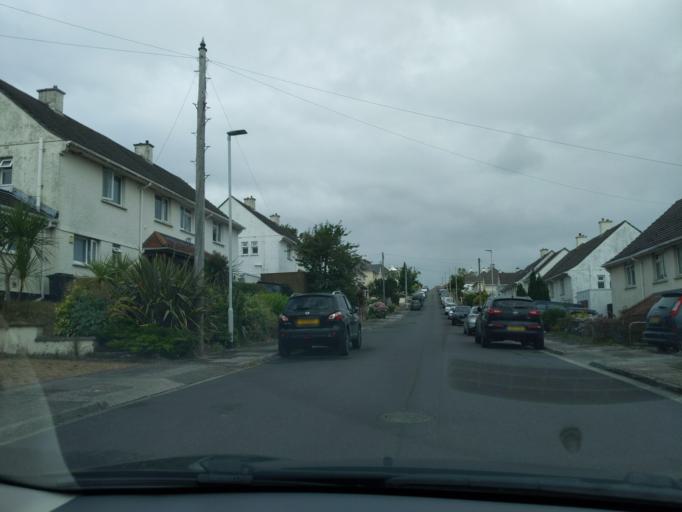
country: GB
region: England
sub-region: Plymouth
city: Plymouth
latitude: 50.3850
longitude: -4.1221
